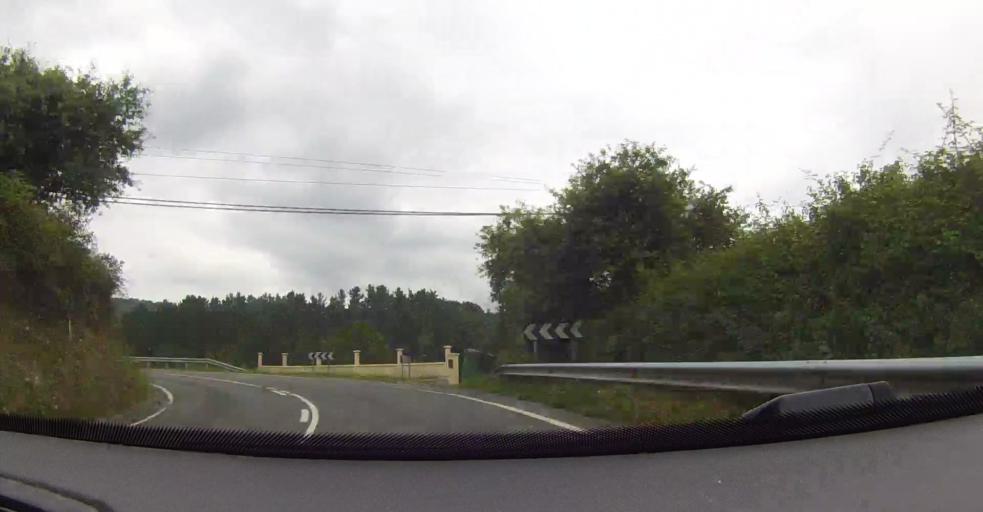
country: ES
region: Basque Country
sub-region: Bizkaia
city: Balmaseda
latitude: 43.2417
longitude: -3.2289
